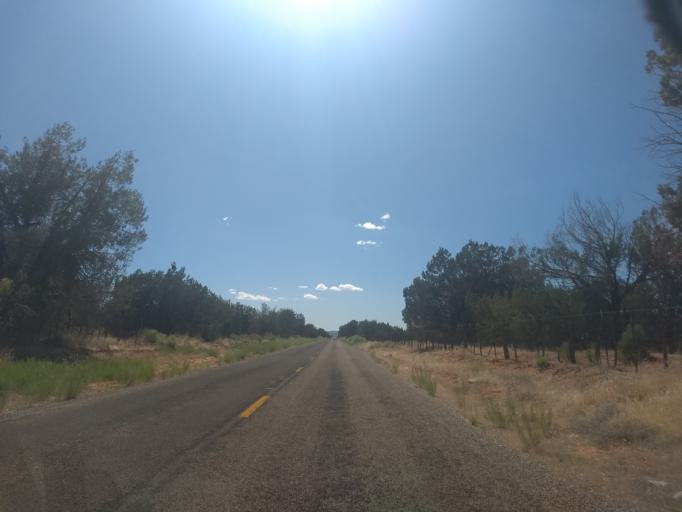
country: US
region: Utah
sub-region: Washington County
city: Hildale
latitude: 36.9468
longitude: -112.8798
